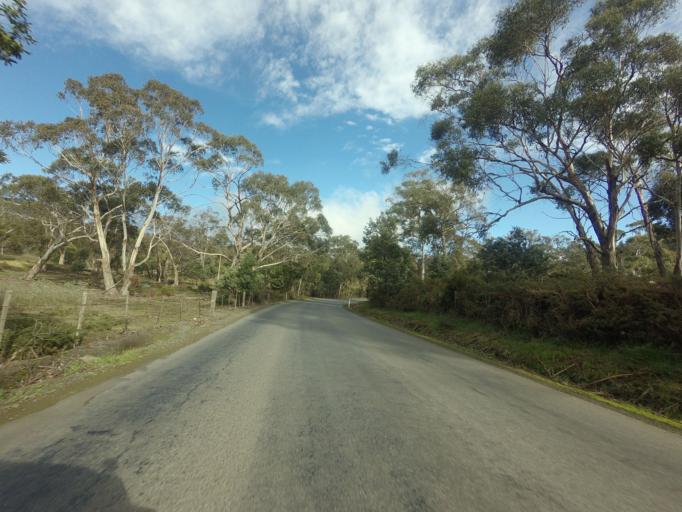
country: AU
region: Tasmania
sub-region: Derwent Valley
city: New Norfolk
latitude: -42.7801
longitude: 147.0152
